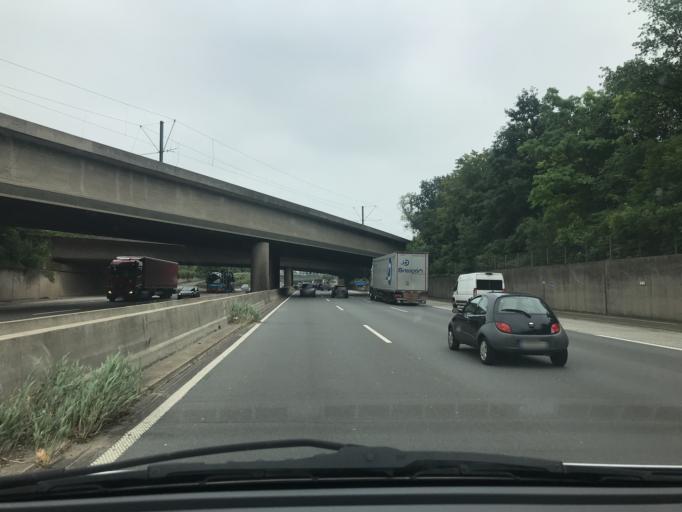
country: DE
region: North Rhine-Westphalia
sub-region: Regierungsbezirk Dusseldorf
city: Dusseldorf
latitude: 51.1927
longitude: 6.8068
